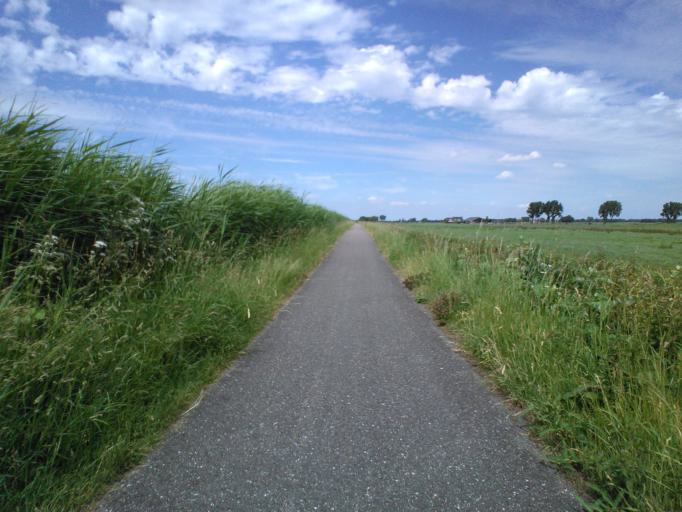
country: NL
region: South Holland
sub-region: Gemeente Giessenlanden
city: Giessenburg
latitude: 51.8566
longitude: 4.8845
